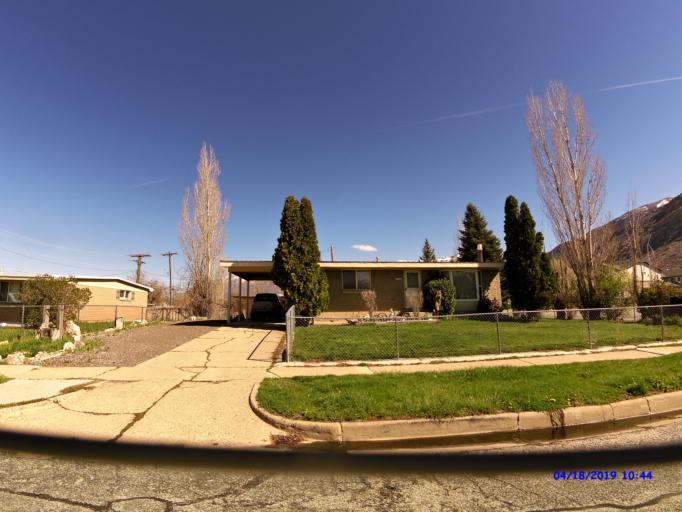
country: US
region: Utah
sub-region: Weber County
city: Harrisville
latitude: 41.2704
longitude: -111.9598
